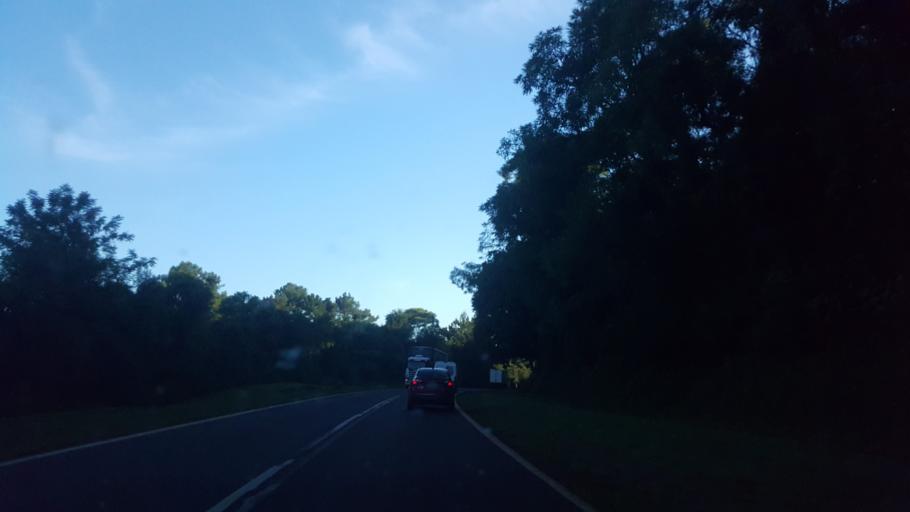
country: AR
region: Misiones
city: El Alcazar
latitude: -26.7558
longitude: -54.8847
